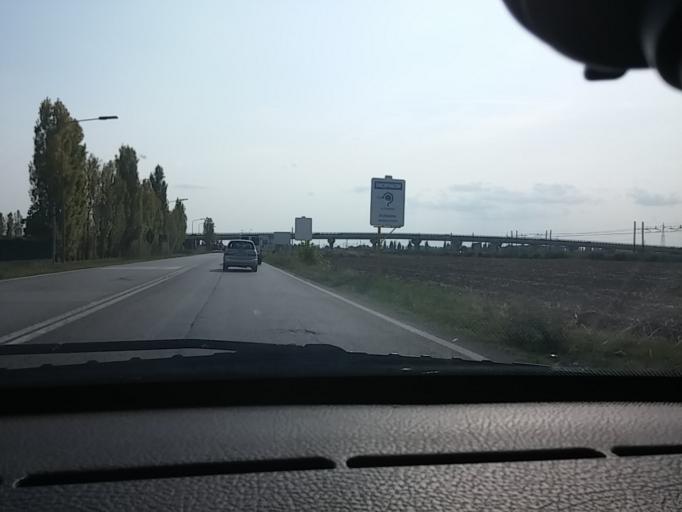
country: IT
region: Emilia-Romagna
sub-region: Provincia di Ferrara
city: Ferrara
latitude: 44.8267
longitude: 11.5919
